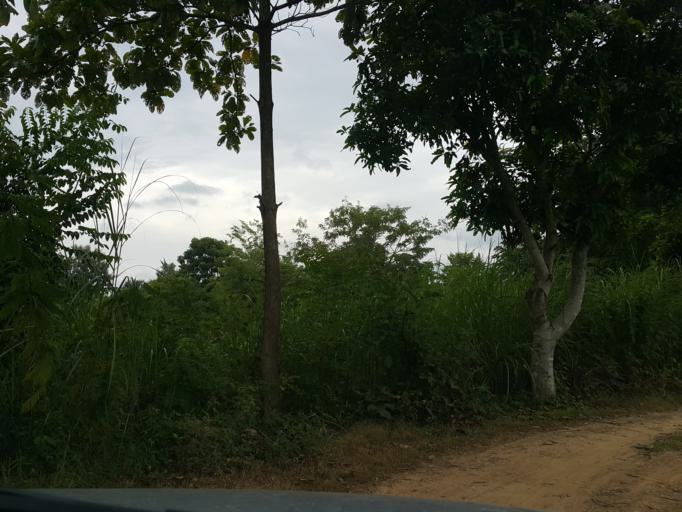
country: TH
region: Chiang Mai
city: San Sai
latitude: 18.8298
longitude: 99.1239
